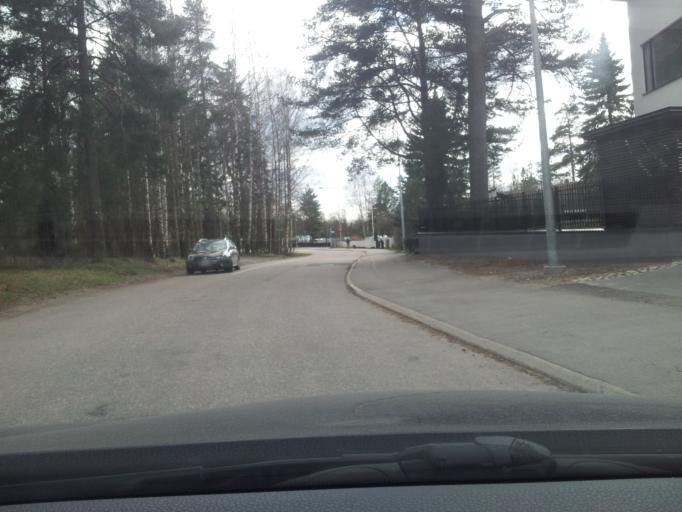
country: FI
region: Uusimaa
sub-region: Helsinki
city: Koukkuniemi
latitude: 60.1759
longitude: 24.7420
